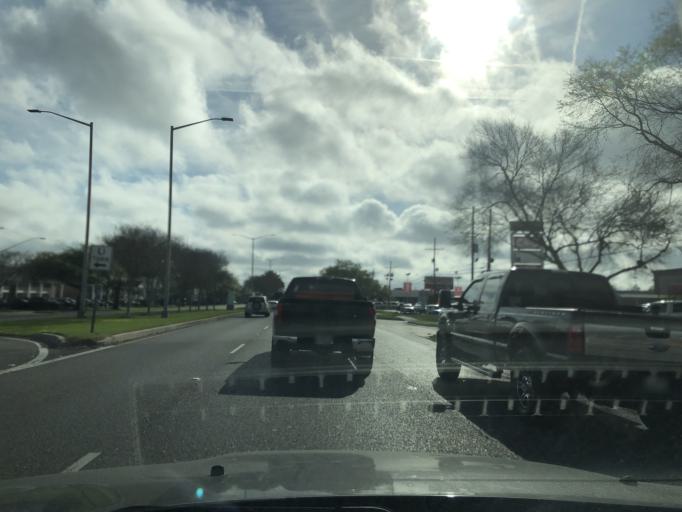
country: US
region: Louisiana
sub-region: Jefferson Parish
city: Kenner
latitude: 30.0050
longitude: -90.2165
